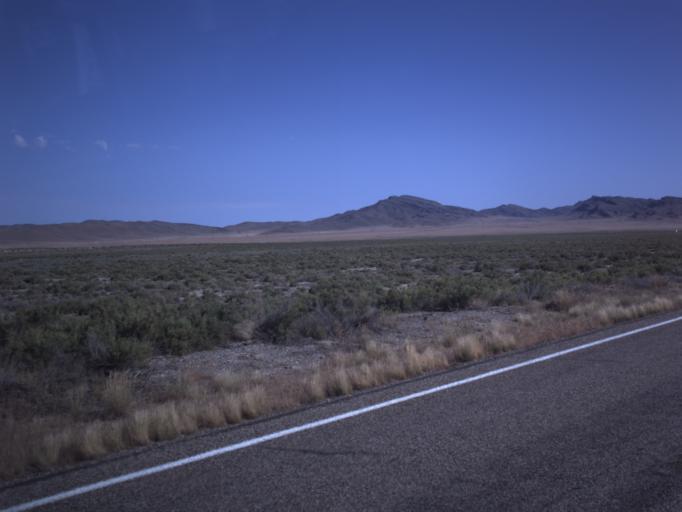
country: US
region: Utah
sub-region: Beaver County
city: Milford
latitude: 38.6923
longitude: -112.9748
